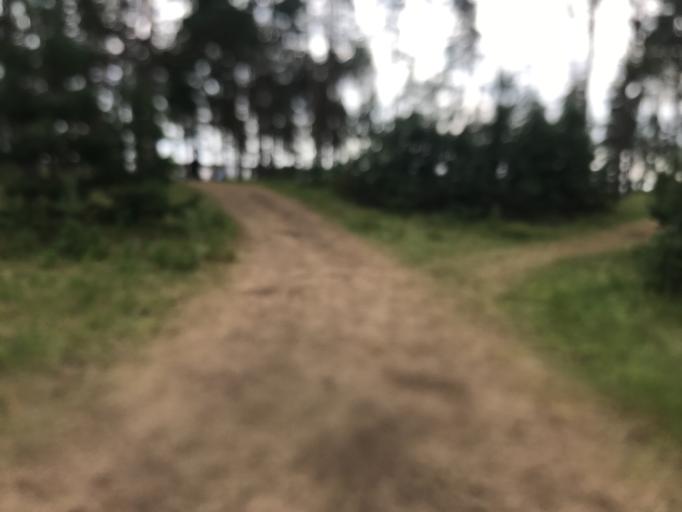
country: SE
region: Skane
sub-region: Kristianstads Kommun
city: Fjalkinge
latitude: 56.0077
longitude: 14.2981
